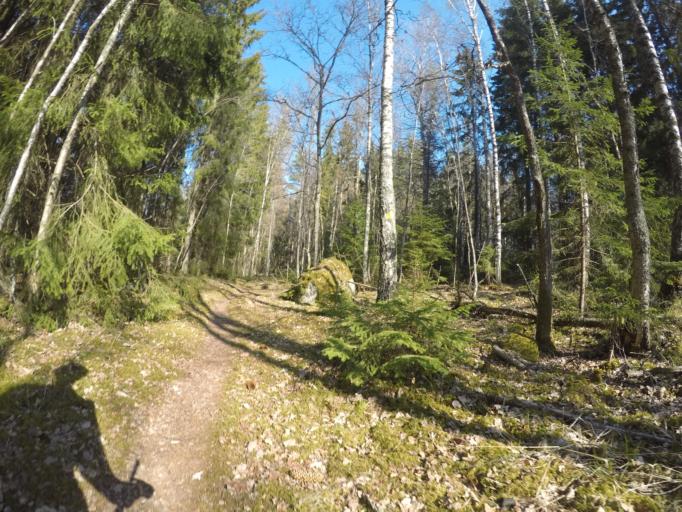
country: SE
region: Vaestmanland
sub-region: Hallstahammars Kommun
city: Kolback
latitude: 59.5356
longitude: 16.2809
